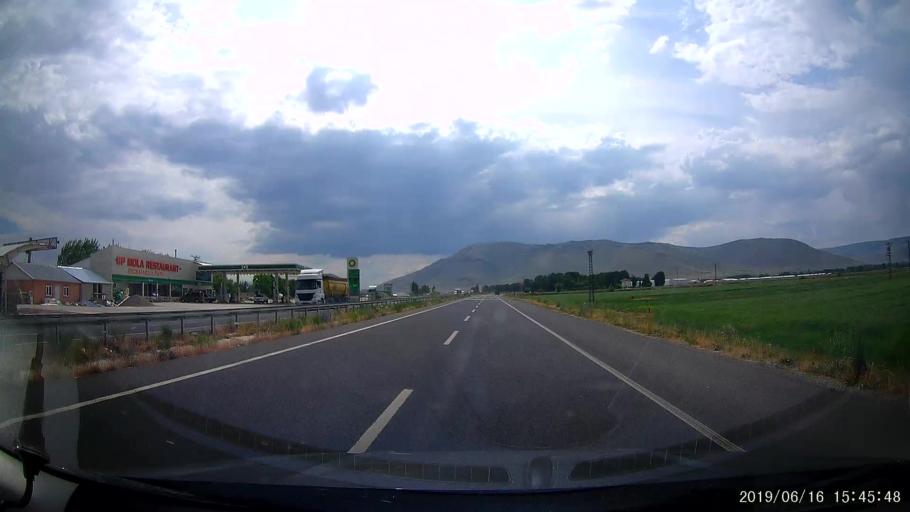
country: TR
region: Erzurum
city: Pasinler
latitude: 39.9893
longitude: 41.7580
